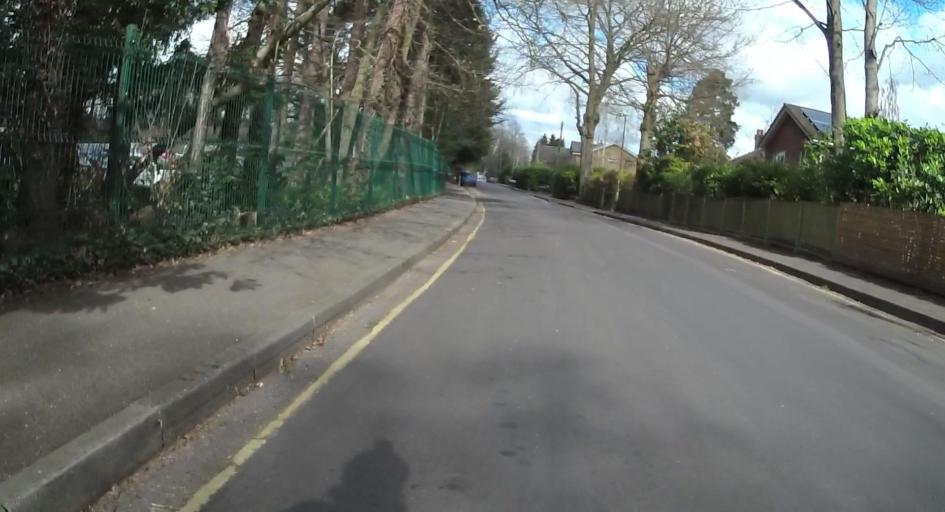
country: GB
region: England
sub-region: Surrey
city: Woking
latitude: 51.3195
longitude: -0.5464
